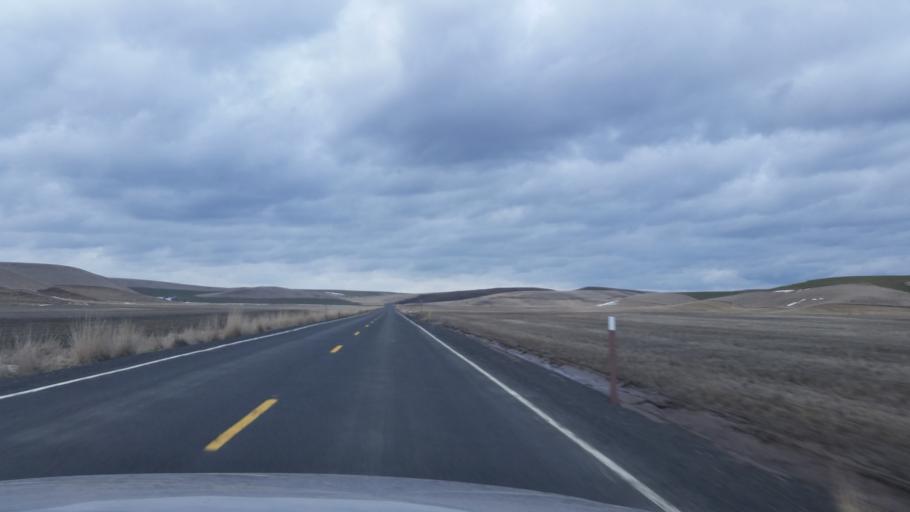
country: US
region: Washington
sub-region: Spokane County
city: Cheney
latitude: 47.1758
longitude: -117.8708
